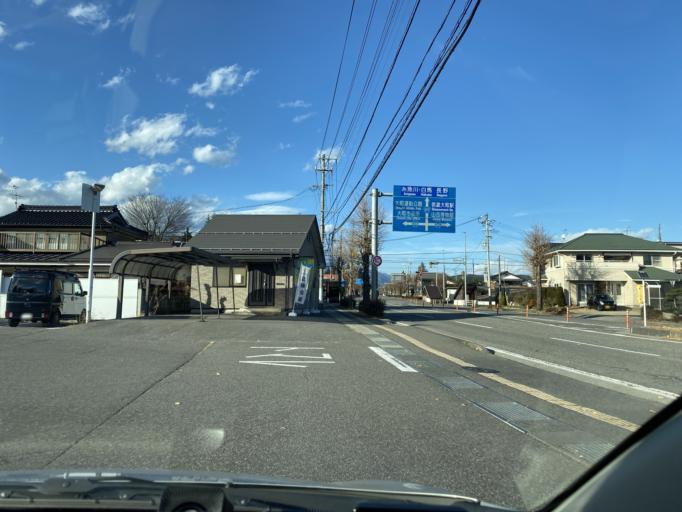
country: JP
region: Nagano
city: Omachi
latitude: 36.5021
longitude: 137.8556
